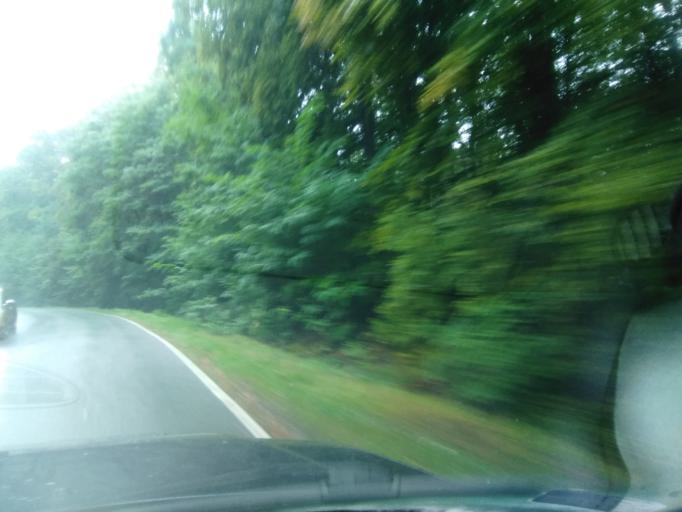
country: PL
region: Subcarpathian Voivodeship
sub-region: Powiat ropczycko-sedziszowski
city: Niedzwiada
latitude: 50.0541
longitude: 21.5360
